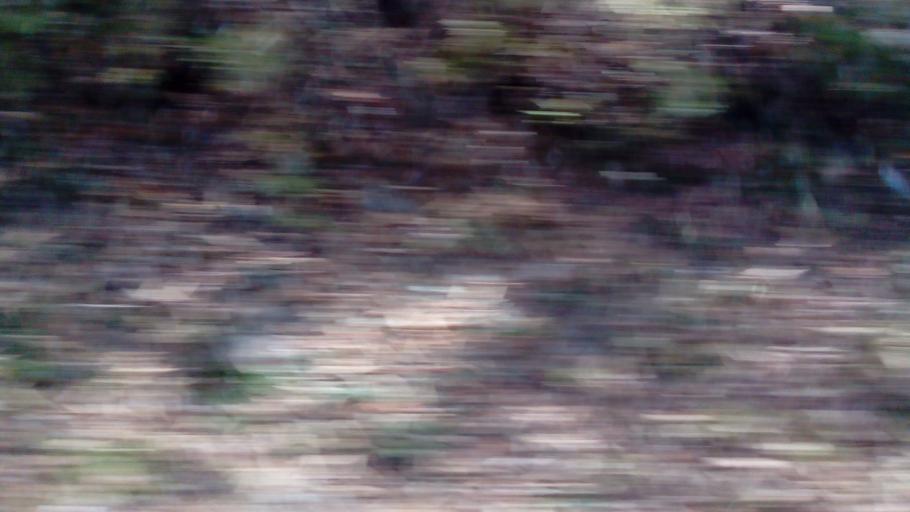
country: TW
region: Taiwan
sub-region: Hualien
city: Hualian
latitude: 24.3648
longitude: 121.3373
